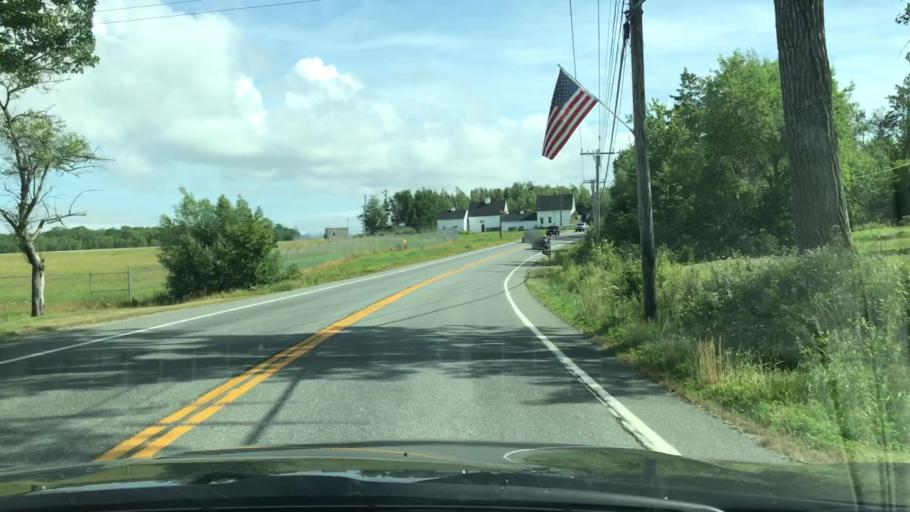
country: US
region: Maine
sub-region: Hancock County
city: Trenton
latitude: 44.4597
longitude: -68.3613
